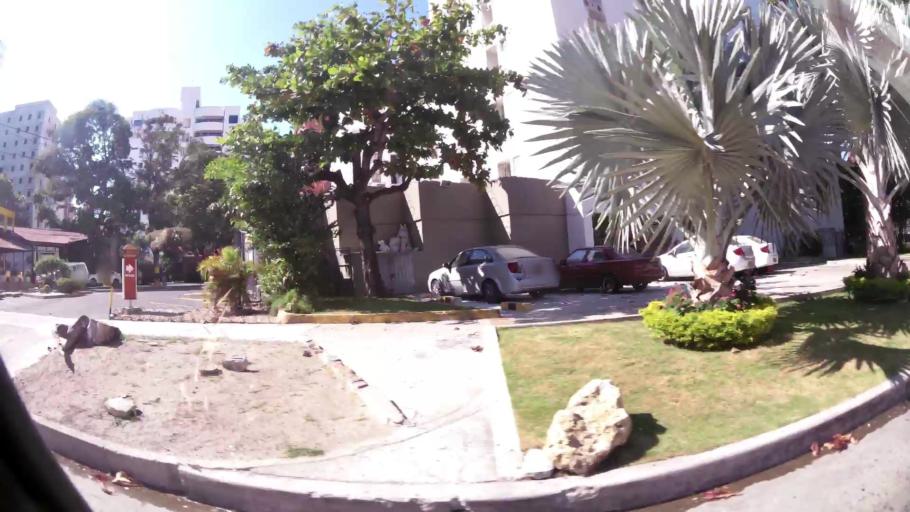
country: CO
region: Atlantico
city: Barranquilla
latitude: 11.0050
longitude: -74.8118
